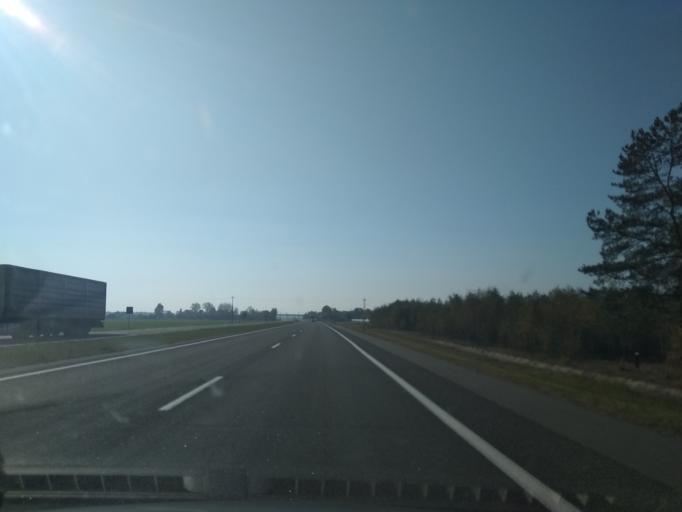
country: BY
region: Brest
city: Antopal'
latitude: 52.3371
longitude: 24.6435
